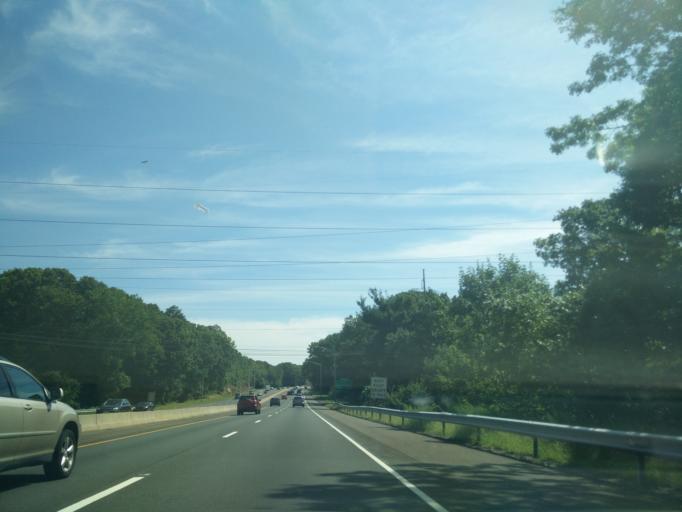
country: US
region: Connecticut
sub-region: New Haven County
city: Branford
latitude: 41.2935
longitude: -72.7952
